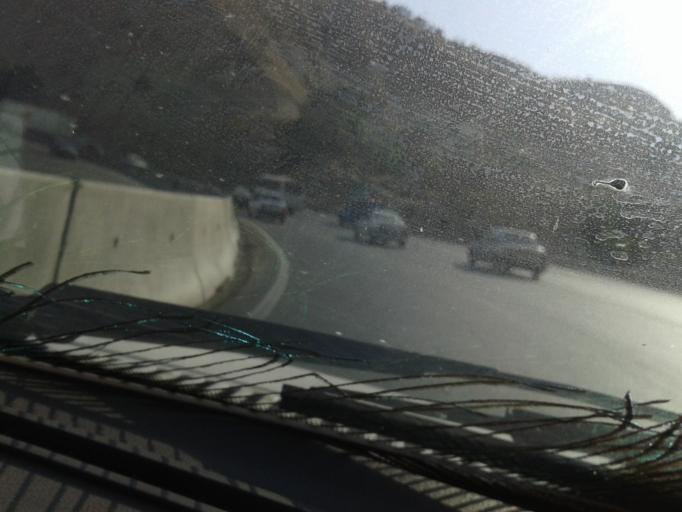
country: IR
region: Tehran
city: Pakdasht
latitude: 35.7349
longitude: 51.6884
